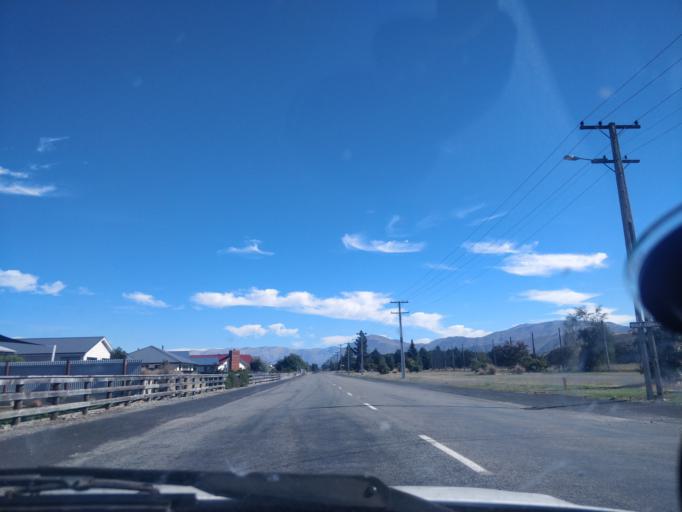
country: NZ
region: Canterbury
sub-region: Timaru District
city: Pleasant Point
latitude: -44.2643
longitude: 170.0953
